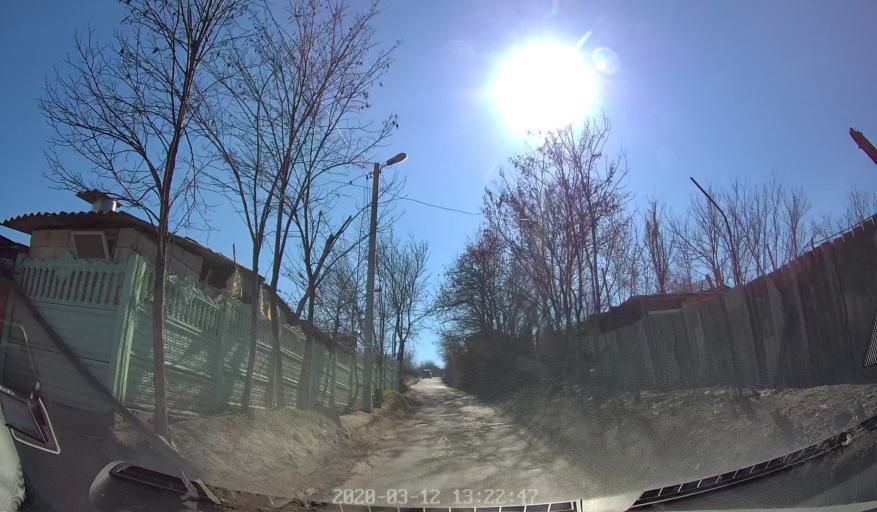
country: MD
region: Laloveni
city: Ialoveni
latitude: 46.9455
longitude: 28.8362
